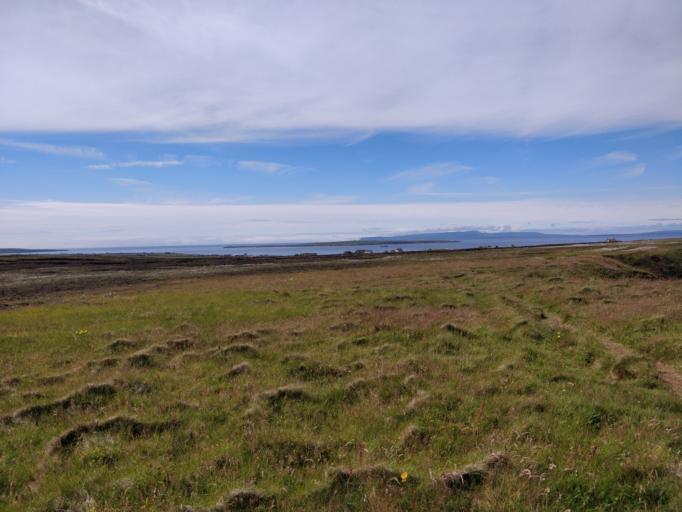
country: GB
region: Scotland
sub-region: Highland
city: Wick
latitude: 58.6314
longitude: -3.0379
